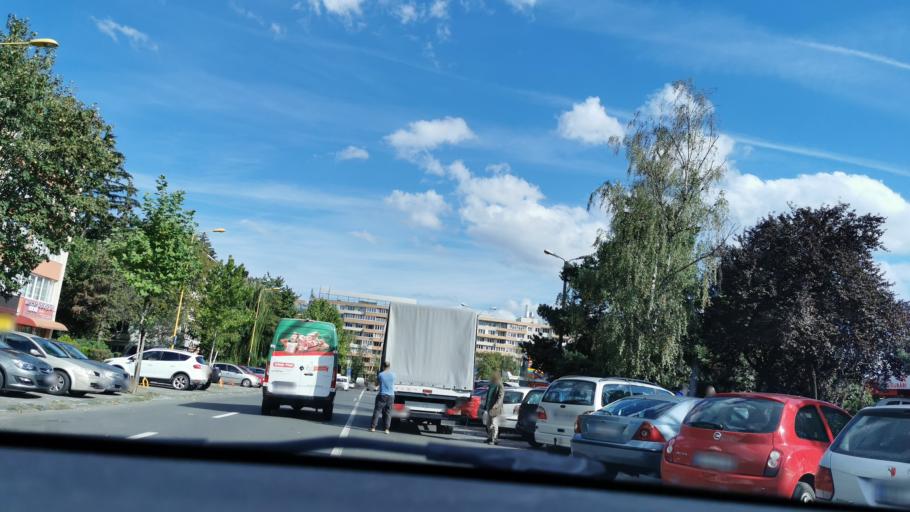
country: RO
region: Brasov
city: Brasov
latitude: 45.6434
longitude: 25.6302
